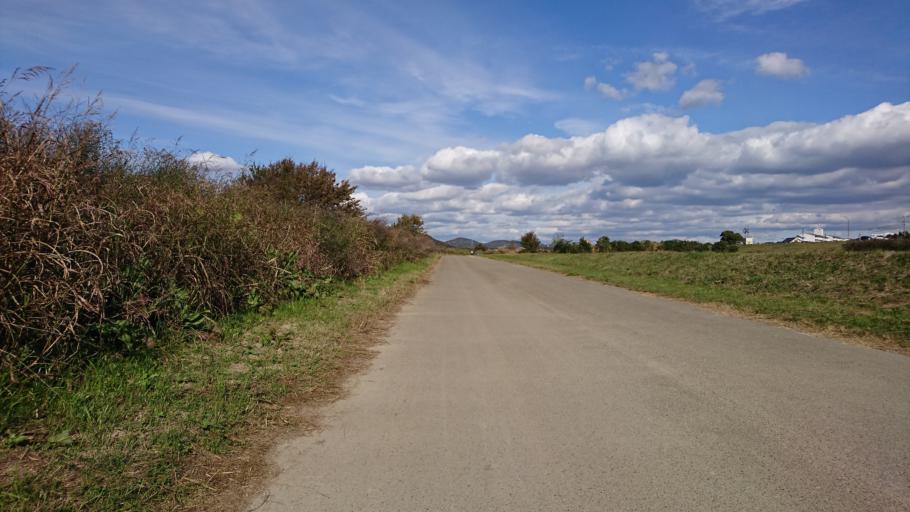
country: JP
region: Hyogo
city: Kakogawacho-honmachi
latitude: 34.7889
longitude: 134.8671
